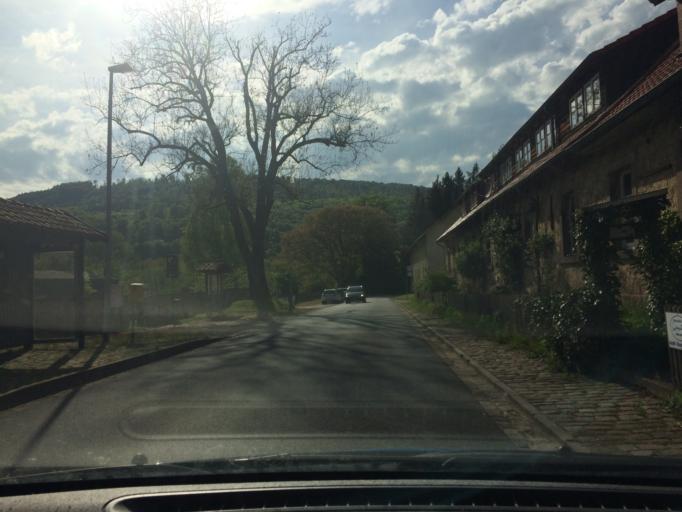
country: DE
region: Lower Saxony
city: Buhren
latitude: 51.5427
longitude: 9.6255
